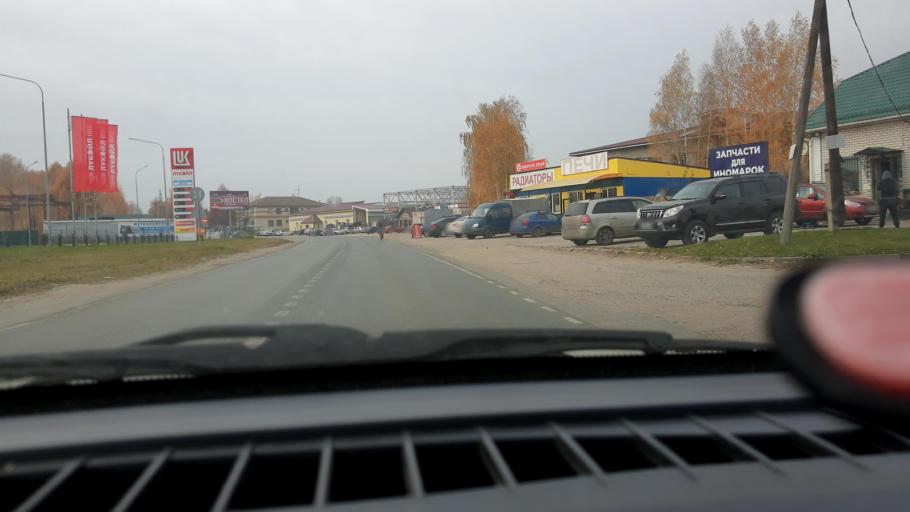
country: RU
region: Nizjnij Novgorod
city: Gorodets
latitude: 56.6405
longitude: 43.5011
